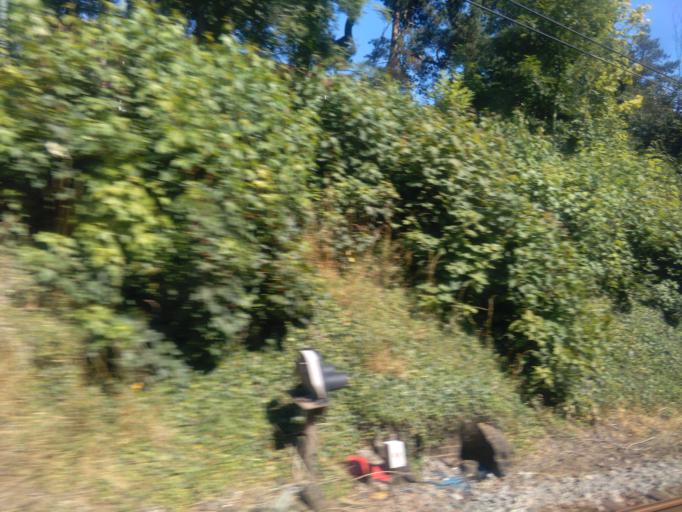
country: GB
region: England
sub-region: Hertfordshire
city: Harpenden
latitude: 51.8176
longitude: -0.3535
